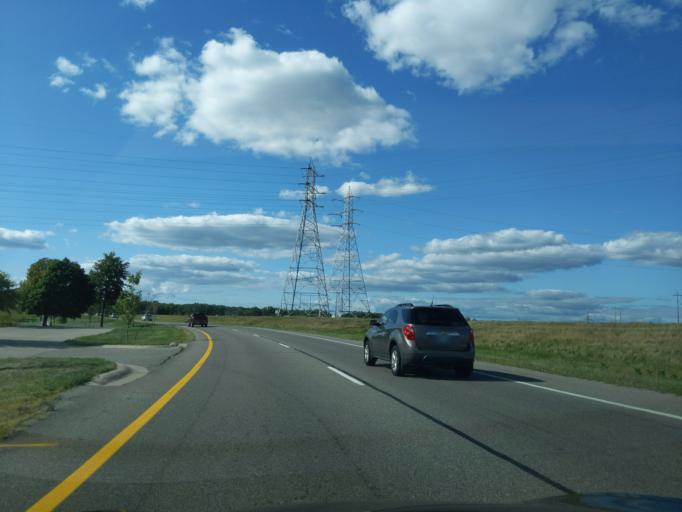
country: US
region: Michigan
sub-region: Muskegon County
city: Muskegon
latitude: 43.2579
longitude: -86.2392
